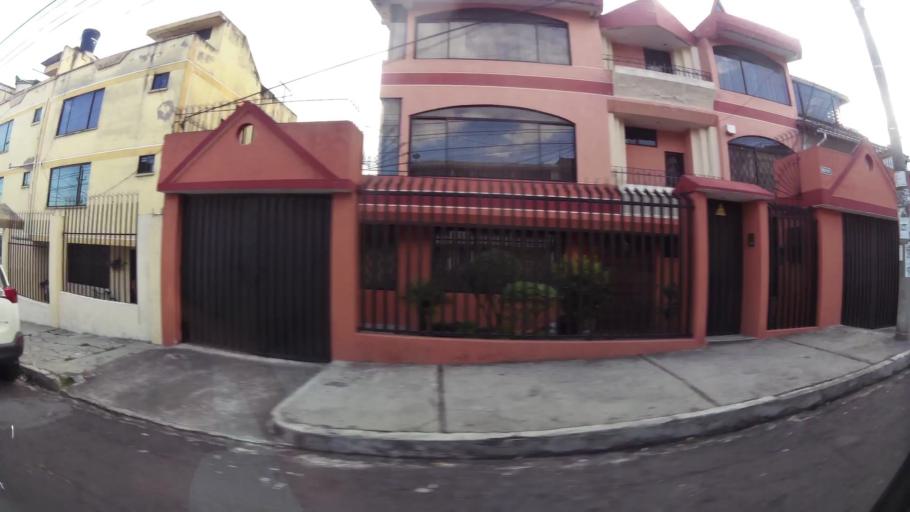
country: EC
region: Pichincha
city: Quito
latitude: -0.1321
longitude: -78.4774
